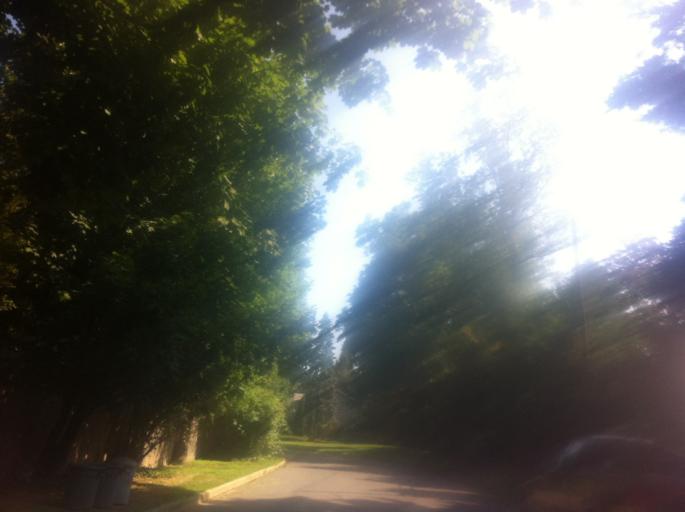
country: US
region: New York
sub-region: Nassau County
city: Glen Cove
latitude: 40.8614
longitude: -73.6135
